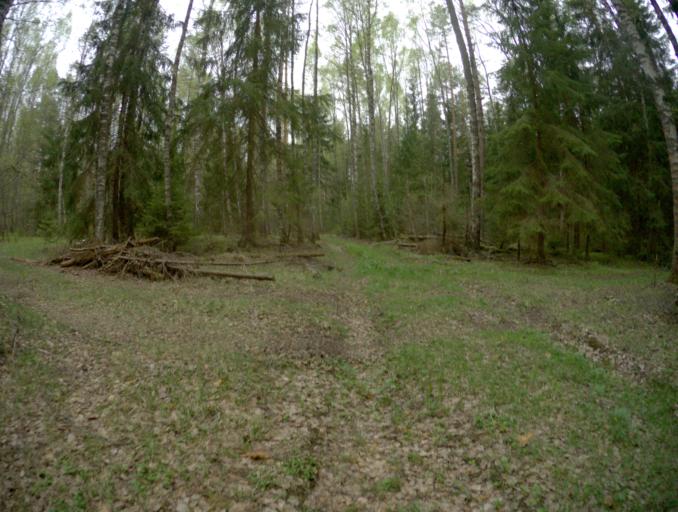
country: RU
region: Vladimir
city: Golovino
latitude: 55.9066
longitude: 40.4567
